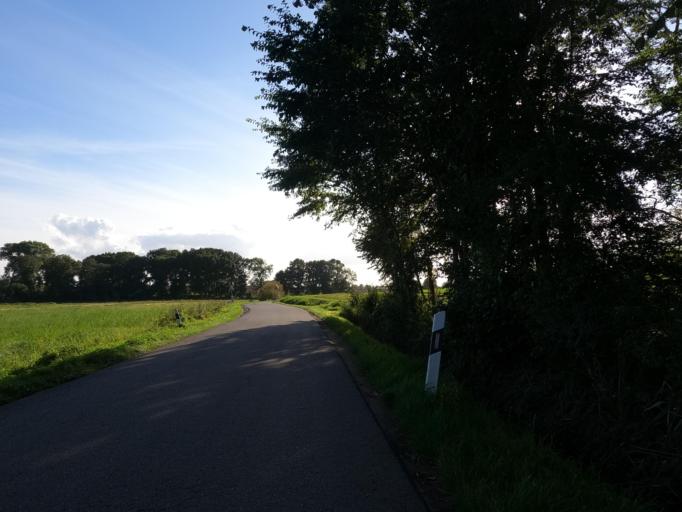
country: DE
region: Schleswig-Holstein
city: Neukirchen
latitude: 54.3347
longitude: 11.0445
